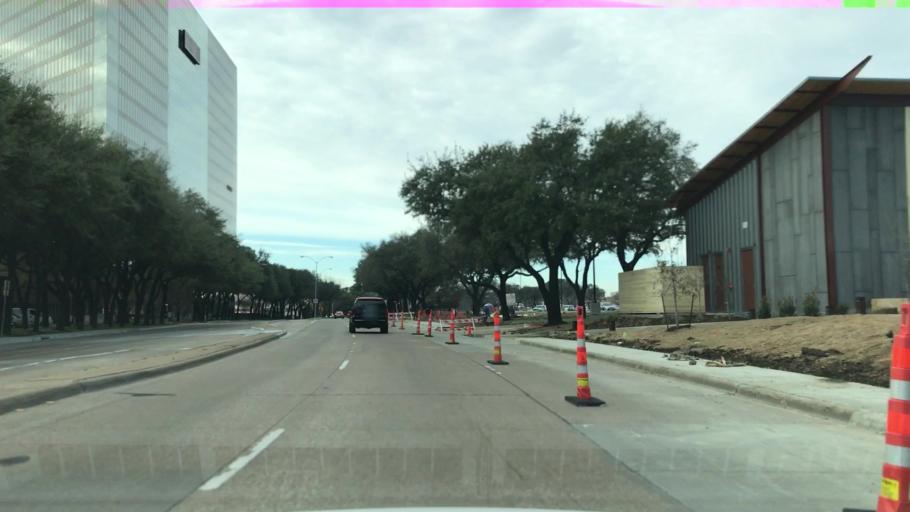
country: US
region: Texas
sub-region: Dallas County
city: University Park
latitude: 32.8824
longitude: -96.7654
